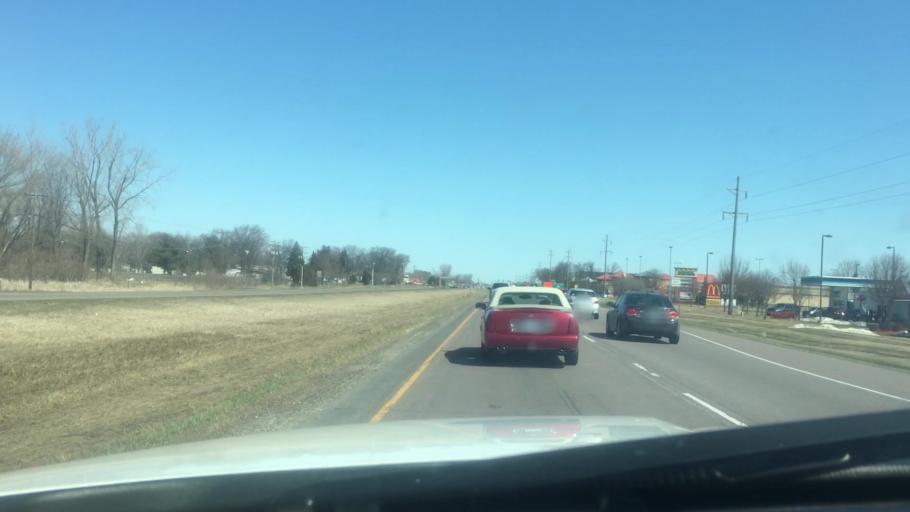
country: US
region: Minnesota
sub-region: Anoka County
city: Blaine
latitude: 45.1557
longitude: -93.2350
